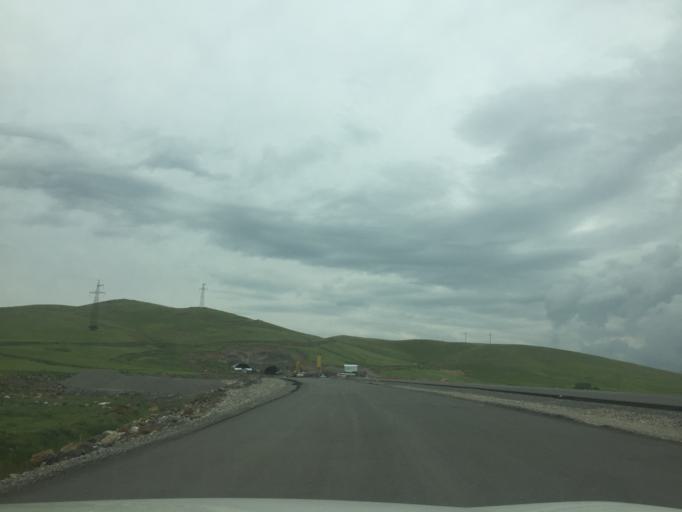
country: KZ
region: Ongtustik Qazaqstan
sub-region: Tulkibas Audany
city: Zhabagly
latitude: 42.5169
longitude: 70.5614
